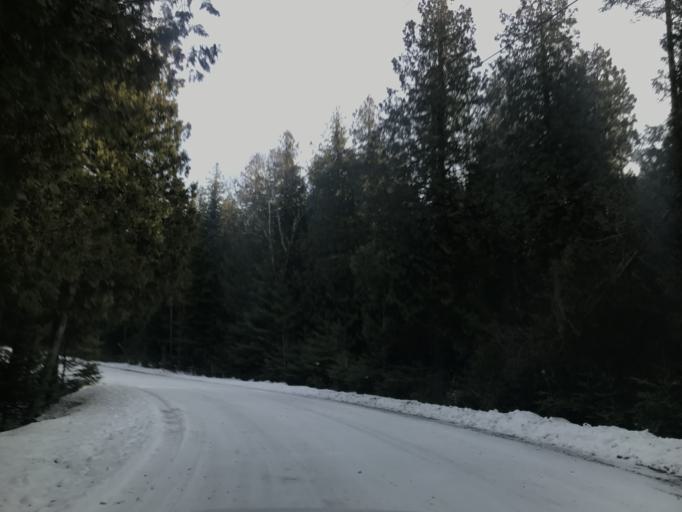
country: US
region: Wisconsin
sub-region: Door County
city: Sturgeon Bay
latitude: 45.1374
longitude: -87.0473
